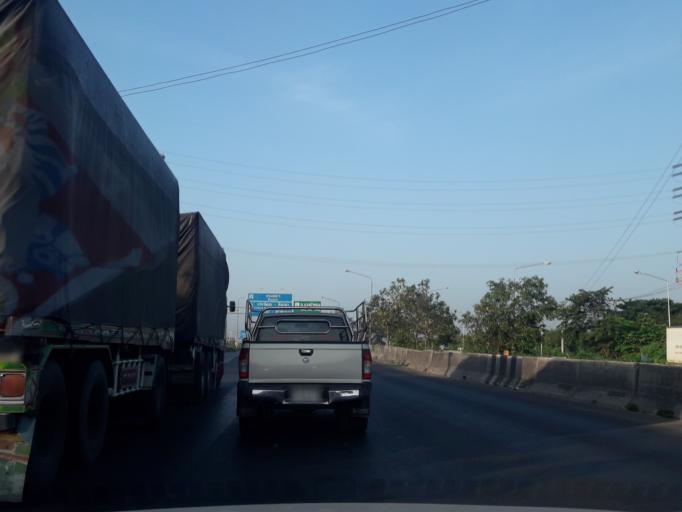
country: TH
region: Phra Nakhon Si Ayutthaya
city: Bang Pa-in
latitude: 14.1519
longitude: 100.5597
